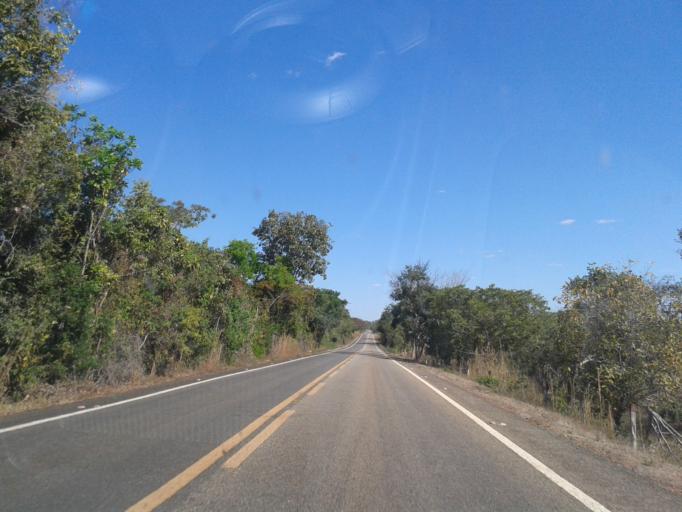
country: BR
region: Goias
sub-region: Sao Miguel Do Araguaia
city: Sao Miguel do Araguaia
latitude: -13.6647
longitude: -50.3254
